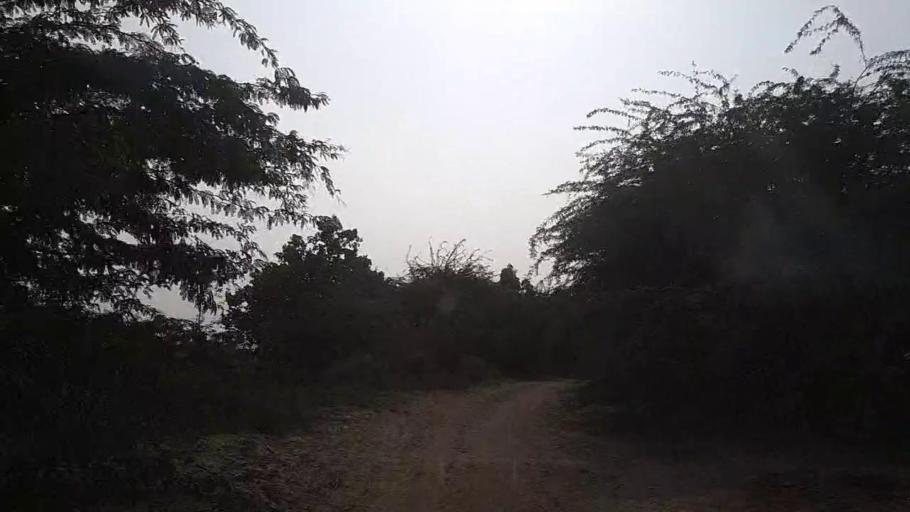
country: PK
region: Sindh
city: Gharo
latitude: 24.6559
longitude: 67.6203
